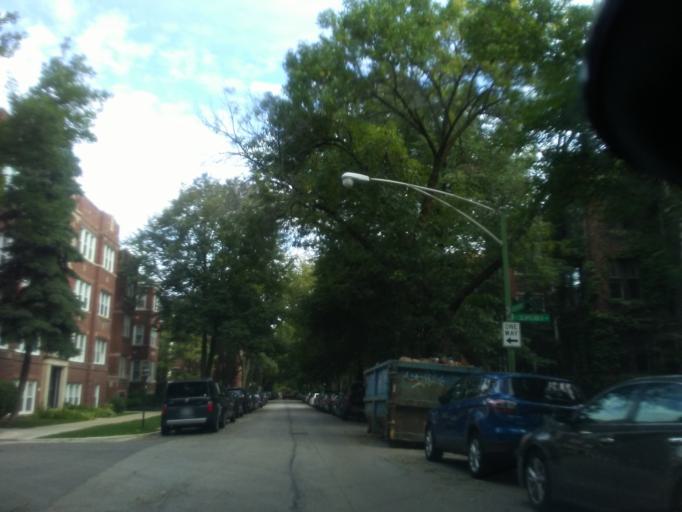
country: US
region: Illinois
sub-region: Cook County
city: Evanston
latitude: 41.9989
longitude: -87.6680
